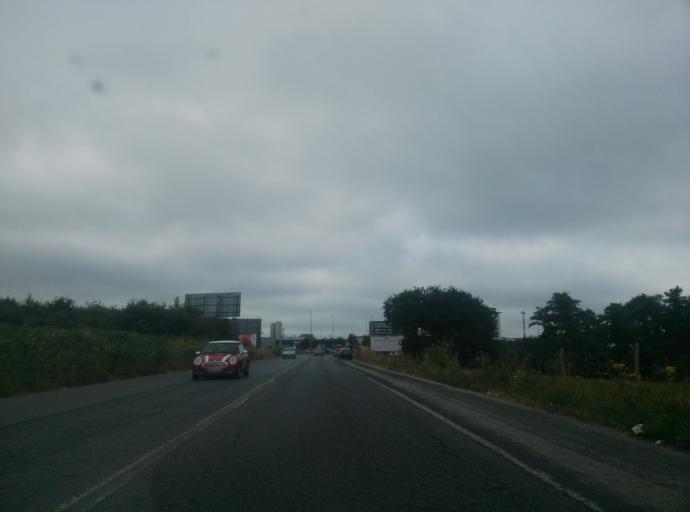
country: ES
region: Galicia
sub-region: Provincia de Lugo
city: Lugo
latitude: 43.0416
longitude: -7.5687
